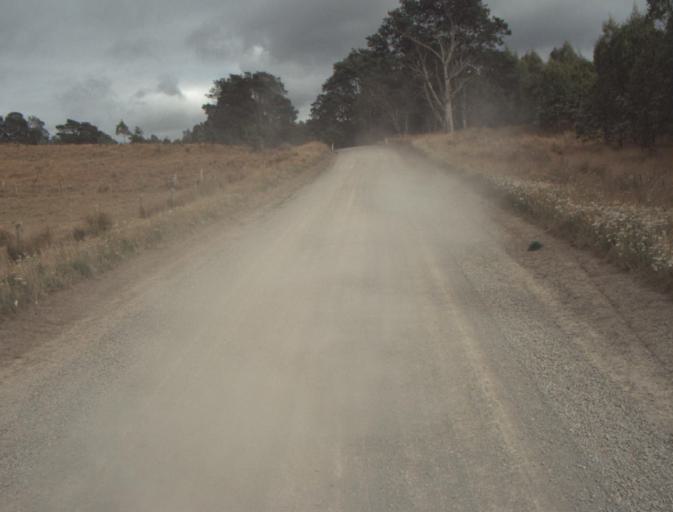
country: AU
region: Tasmania
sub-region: Dorset
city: Scottsdale
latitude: -41.3476
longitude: 147.4471
